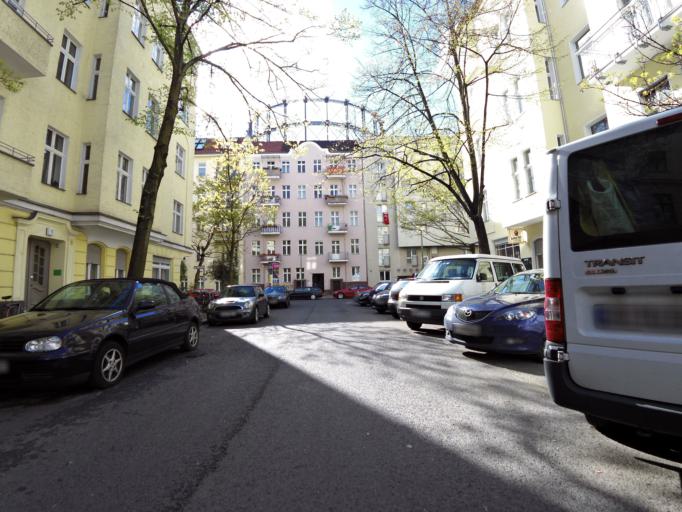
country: DE
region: Berlin
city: Berlin Schoeneberg
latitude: 52.4814
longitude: 13.3595
